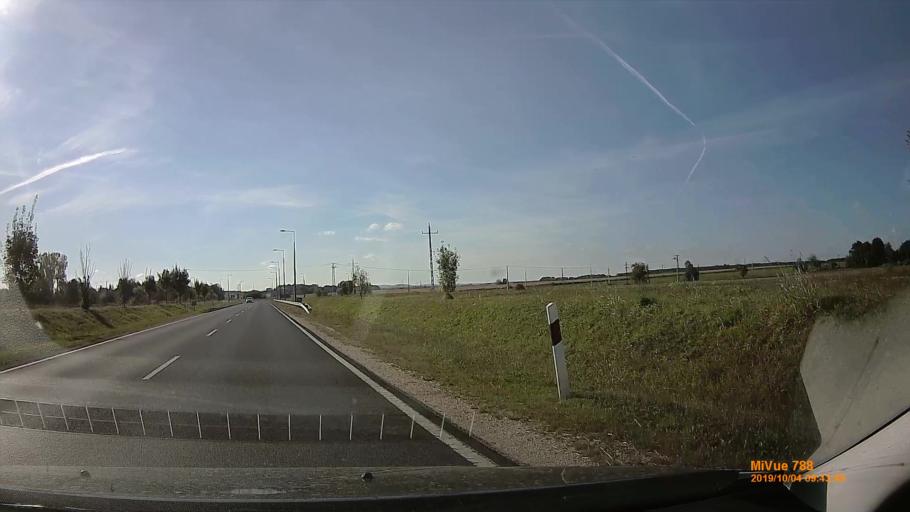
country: HU
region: Somogy
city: Kaposvar
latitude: 46.4156
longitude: 17.7695
